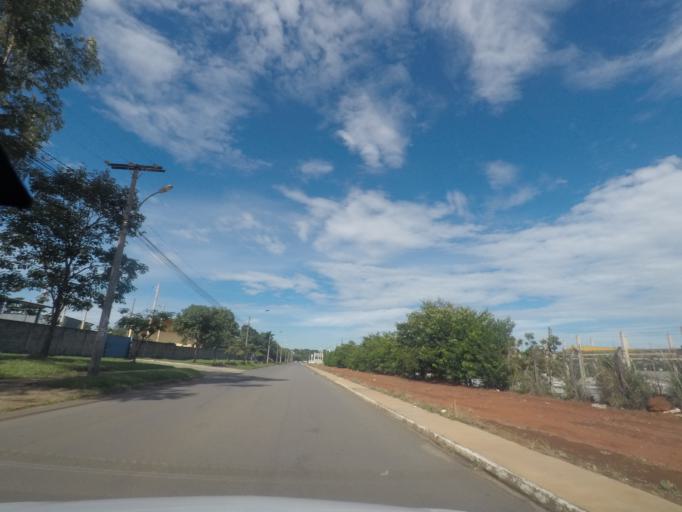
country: BR
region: Goias
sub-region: Aparecida De Goiania
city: Aparecida de Goiania
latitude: -16.7909
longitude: -49.2587
